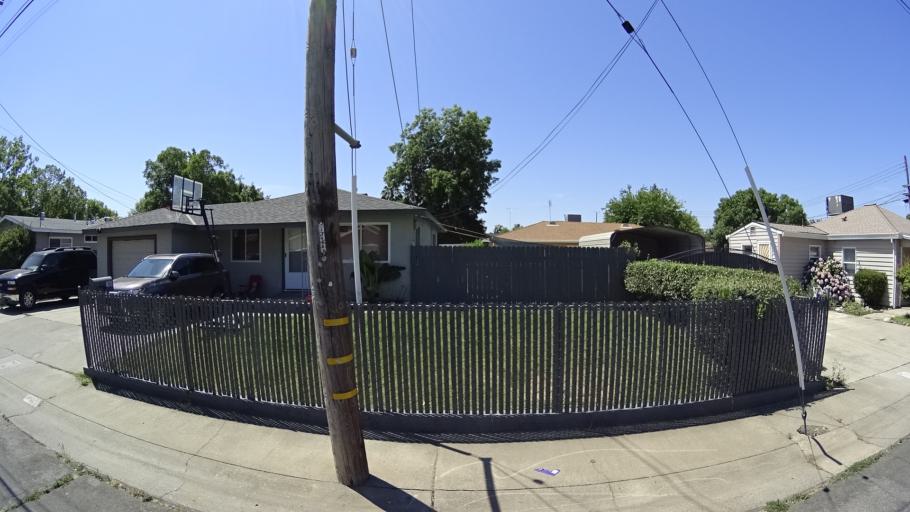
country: US
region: California
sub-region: Sacramento County
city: Florin
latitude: 38.5359
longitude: -121.4158
